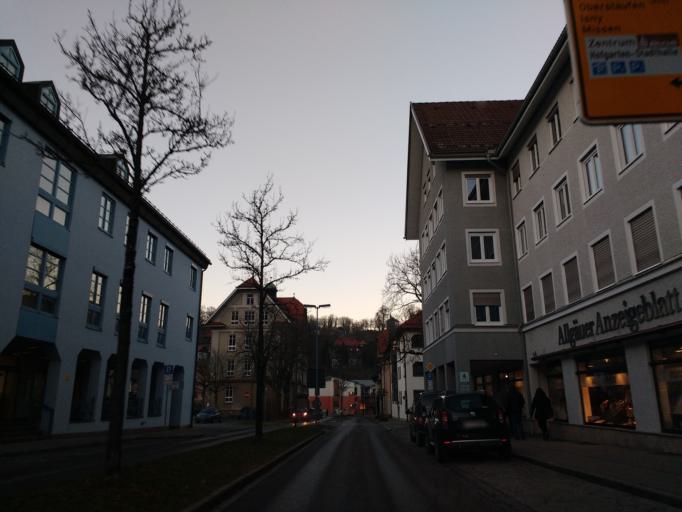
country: DE
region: Bavaria
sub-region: Swabia
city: Immenstadt im Allgau
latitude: 47.5597
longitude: 10.2210
